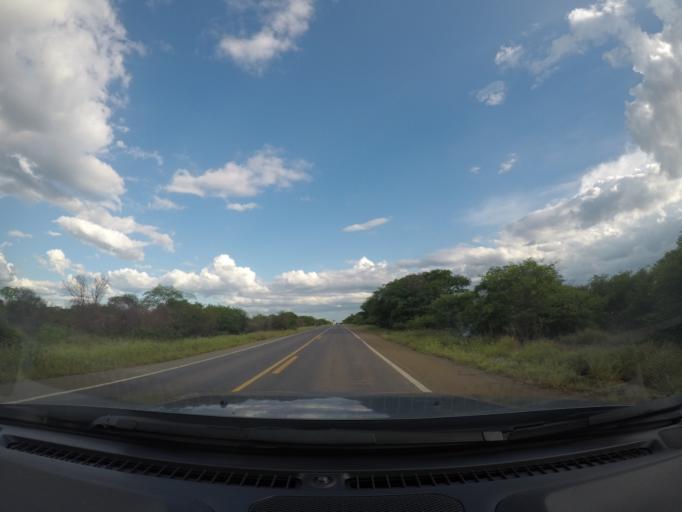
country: BR
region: Bahia
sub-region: Oliveira Dos Brejinhos
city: Beira Rio
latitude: -12.1902
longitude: -42.8242
